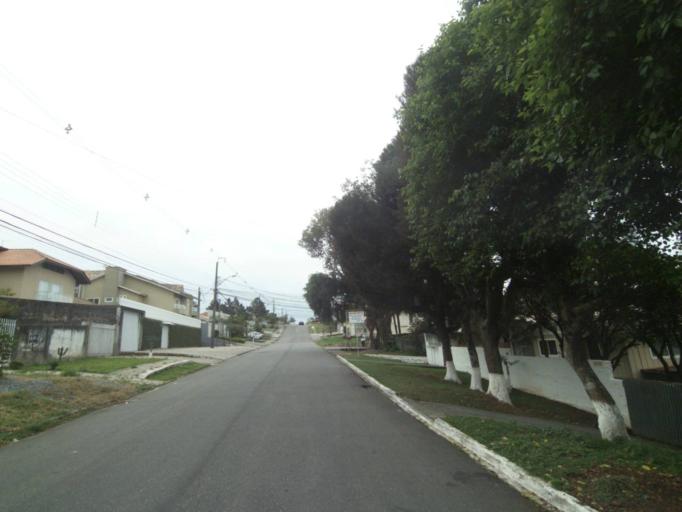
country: BR
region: Parana
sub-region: Pinhais
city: Pinhais
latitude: -25.4215
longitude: -49.2059
